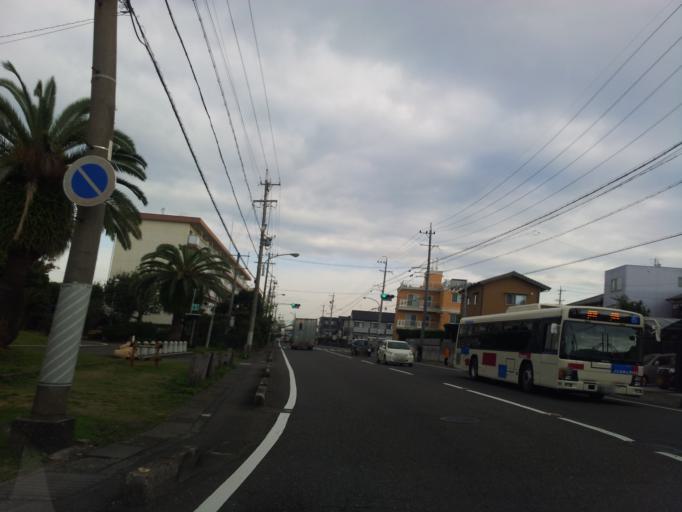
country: JP
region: Shizuoka
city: Shizuoka-shi
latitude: 34.9870
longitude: 138.5097
